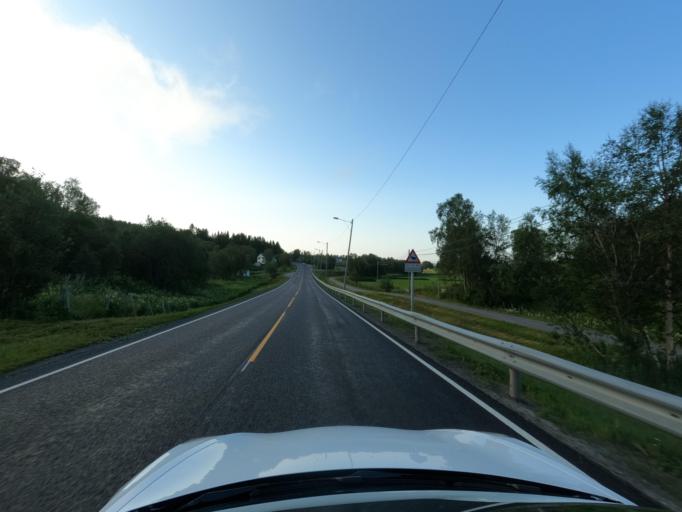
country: NO
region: Troms
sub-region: Skanland
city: Evenskjer
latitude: 68.6669
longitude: 16.5759
